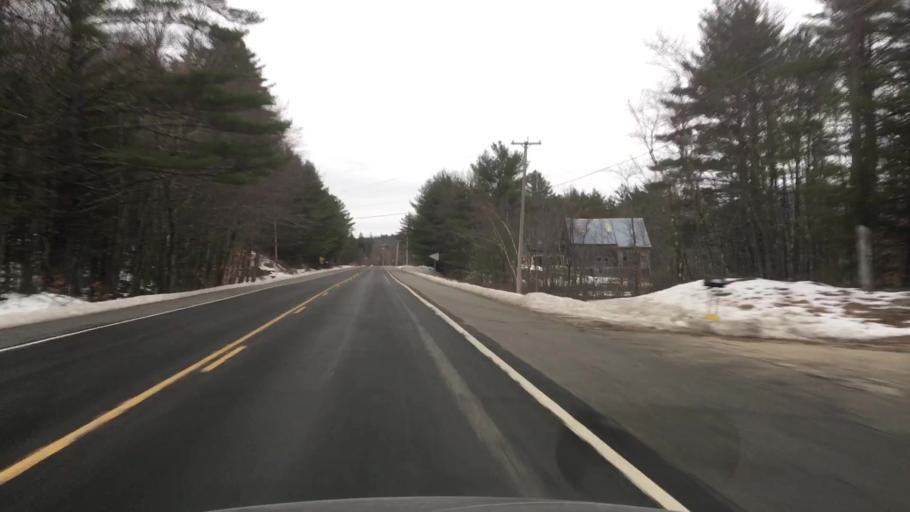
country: US
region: New Hampshire
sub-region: Merrimack County
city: Henniker
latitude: 43.2198
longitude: -71.8807
